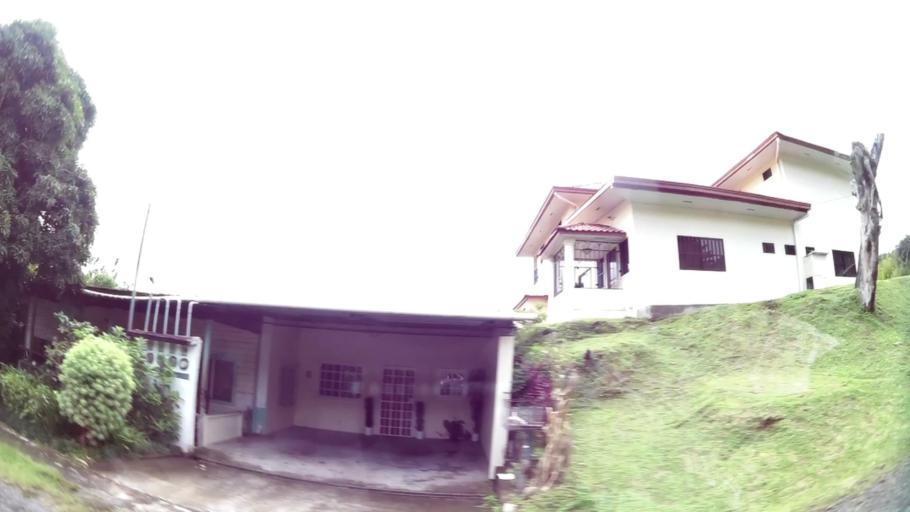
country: PA
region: Chiriqui
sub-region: Distrito Boquete
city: Boquete
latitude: 8.7777
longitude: -82.4343
